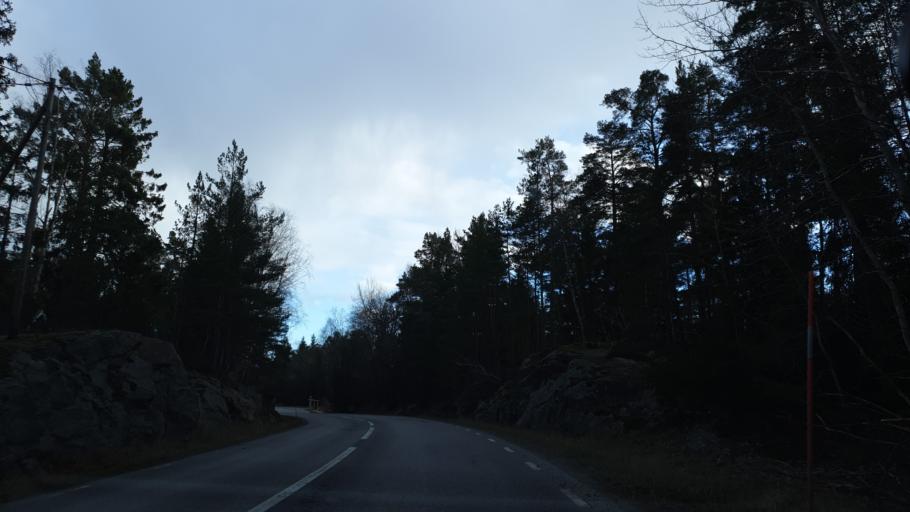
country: SE
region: Stockholm
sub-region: Varmdo Kommun
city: Holo
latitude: 59.3377
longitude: 18.7174
